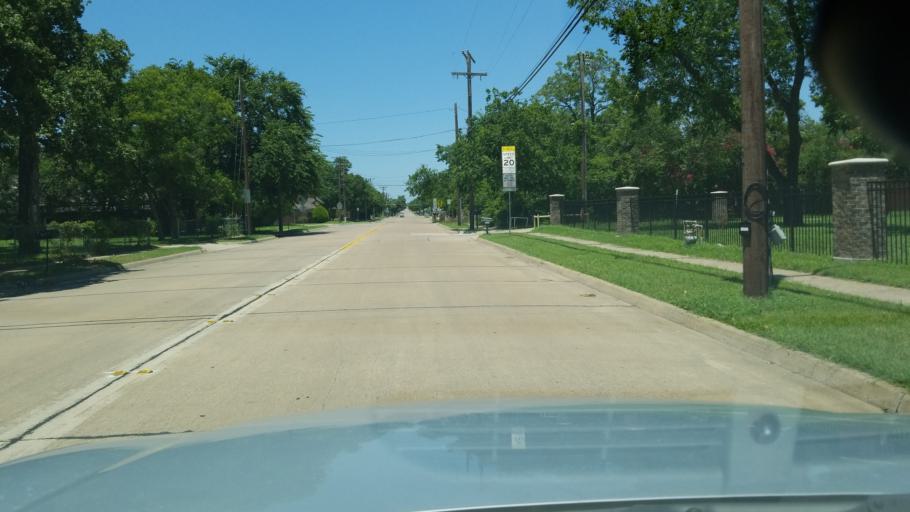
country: US
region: Texas
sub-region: Dallas County
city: Irving
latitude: 32.7980
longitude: -96.9257
